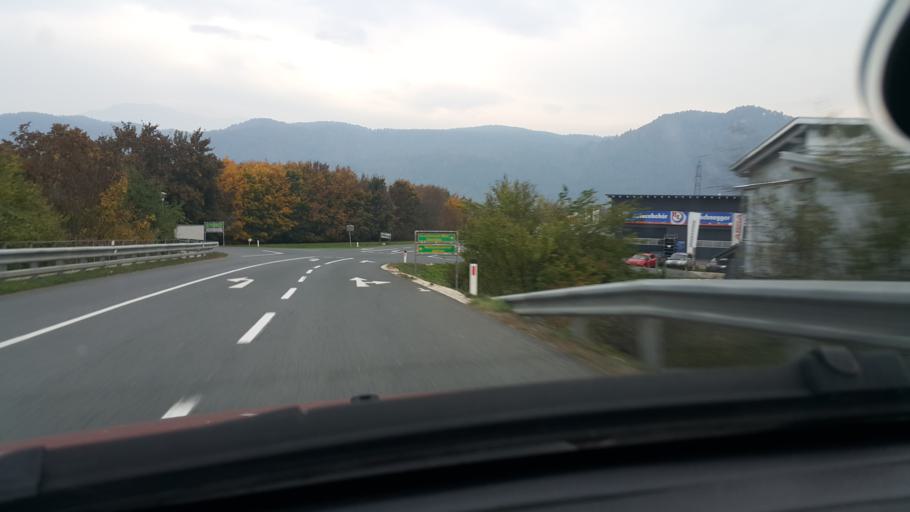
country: AT
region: Carinthia
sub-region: Politischer Bezirk Klagenfurt Land
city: Ebenthal
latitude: 46.6186
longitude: 14.3993
